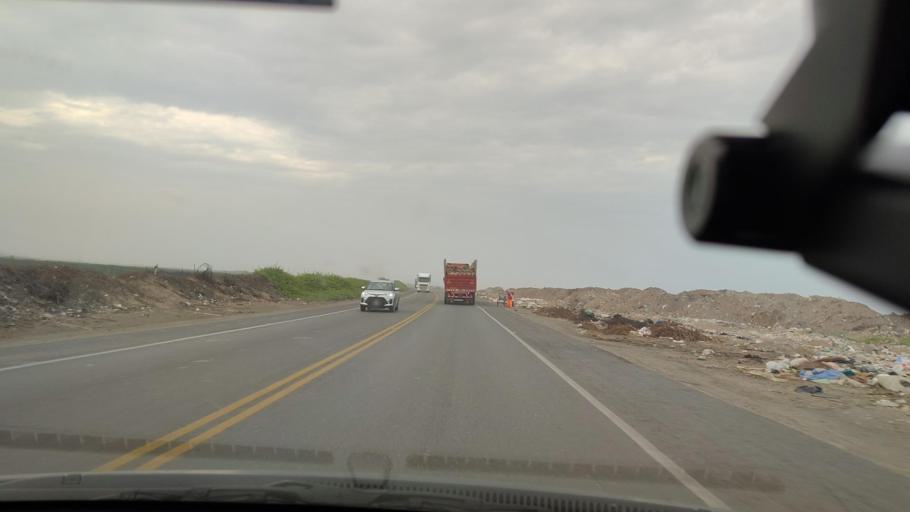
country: PE
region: La Libertad
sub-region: Provincia de Trujillo
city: Huanchaco
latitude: -8.1077
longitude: -79.0974
